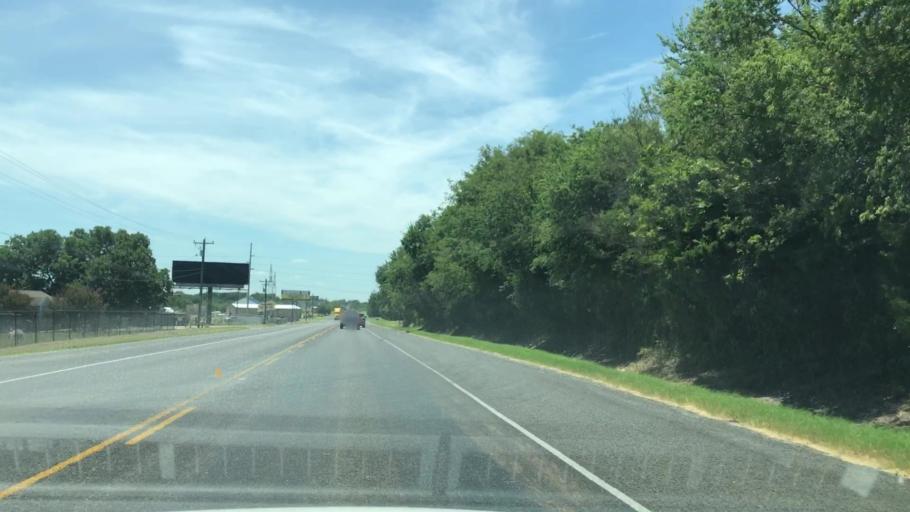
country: US
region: Texas
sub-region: Collin County
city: Lavon
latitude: 33.0111
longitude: -96.4585
